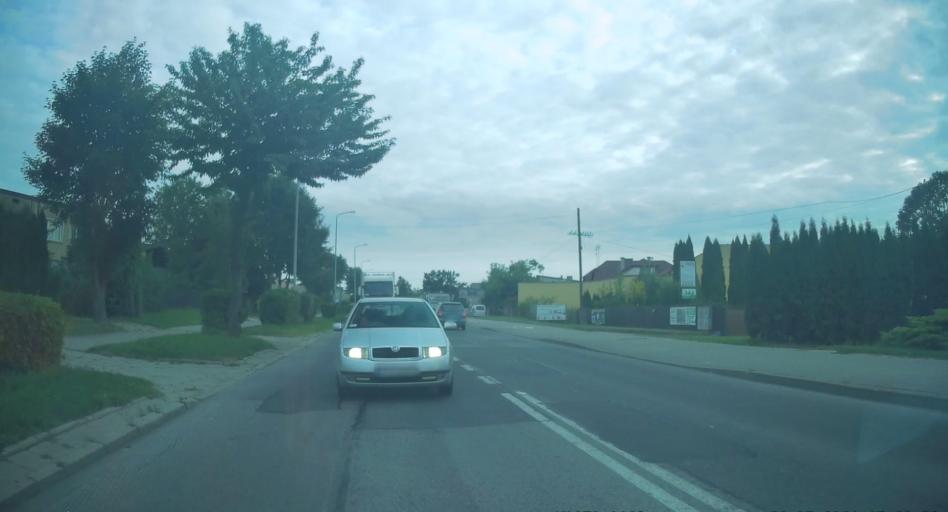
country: PL
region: Lodz Voivodeship
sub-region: Powiat radomszczanski
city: Radomsko
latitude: 51.0589
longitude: 19.4413
